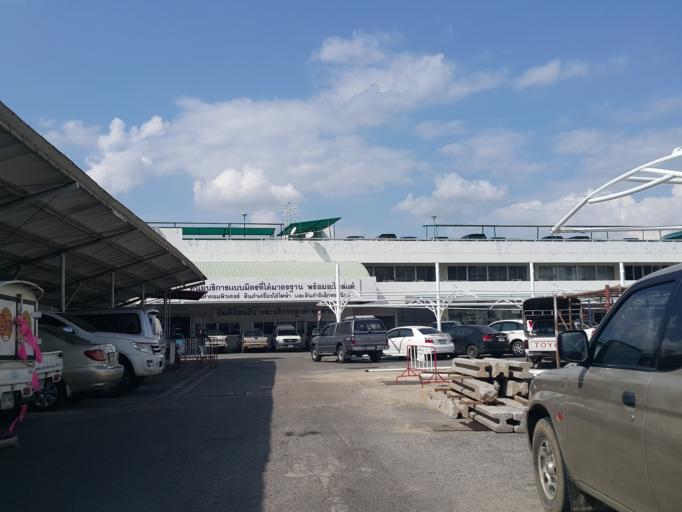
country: TH
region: Chiang Mai
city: Chiang Mai
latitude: 18.7739
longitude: 98.9752
